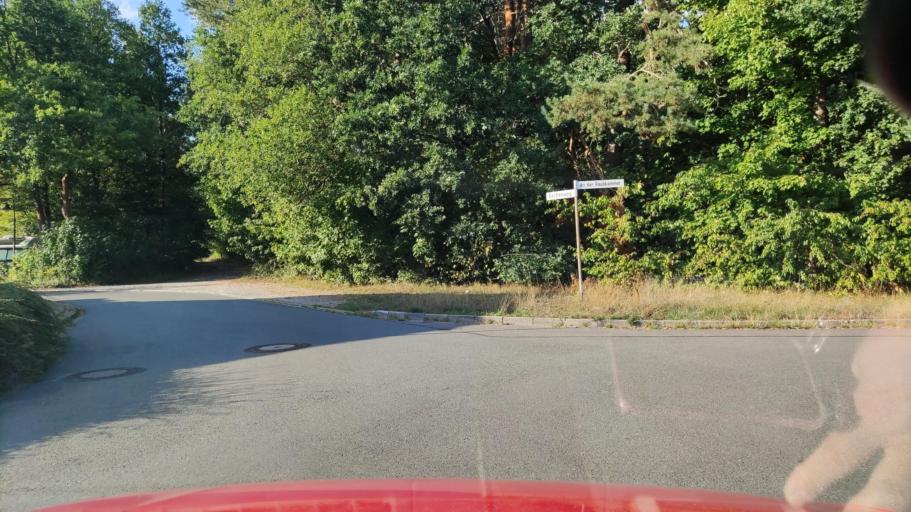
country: DE
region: Lower Saxony
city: Munster
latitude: 53.0050
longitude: 10.1038
